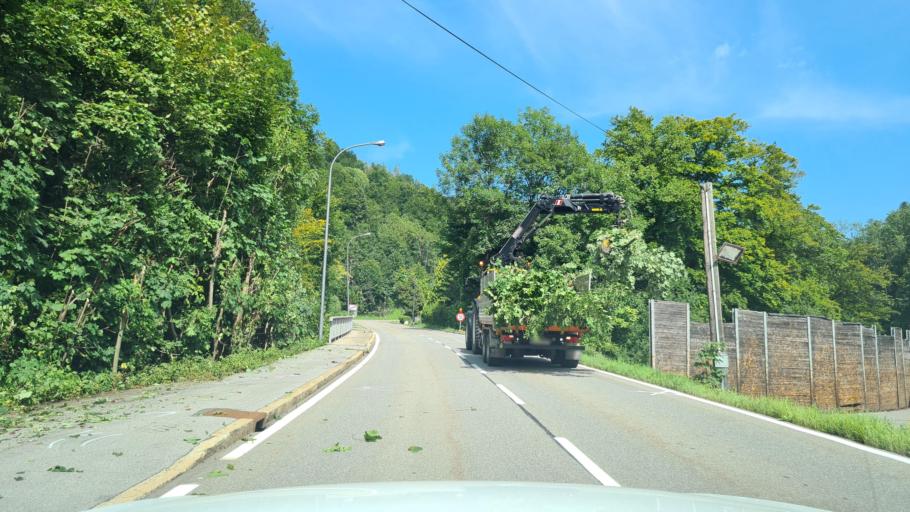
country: AT
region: Vorarlberg
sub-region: Politischer Bezirk Bregenz
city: Bildstein
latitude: 47.4446
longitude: 9.7707
